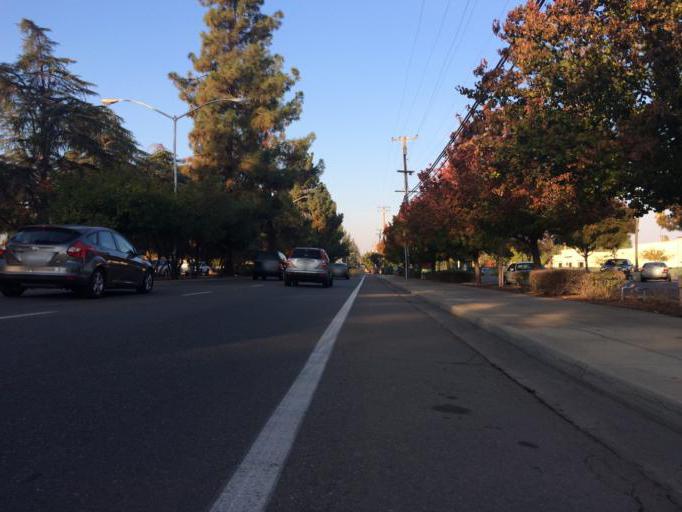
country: US
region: California
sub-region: Fresno County
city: Fresno
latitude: 36.7942
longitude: -119.7563
